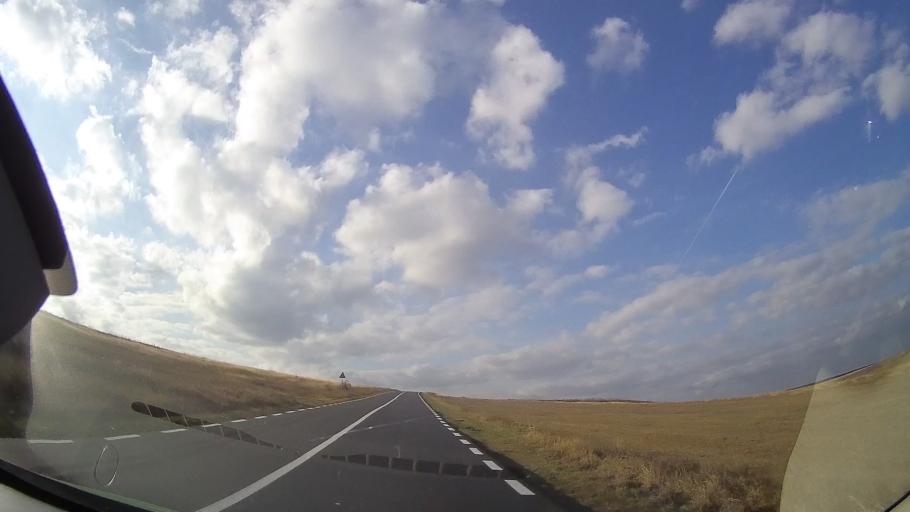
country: RO
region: Constanta
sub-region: Comuna Albesti
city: Albesti
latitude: 43.8084
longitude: 28.4175
